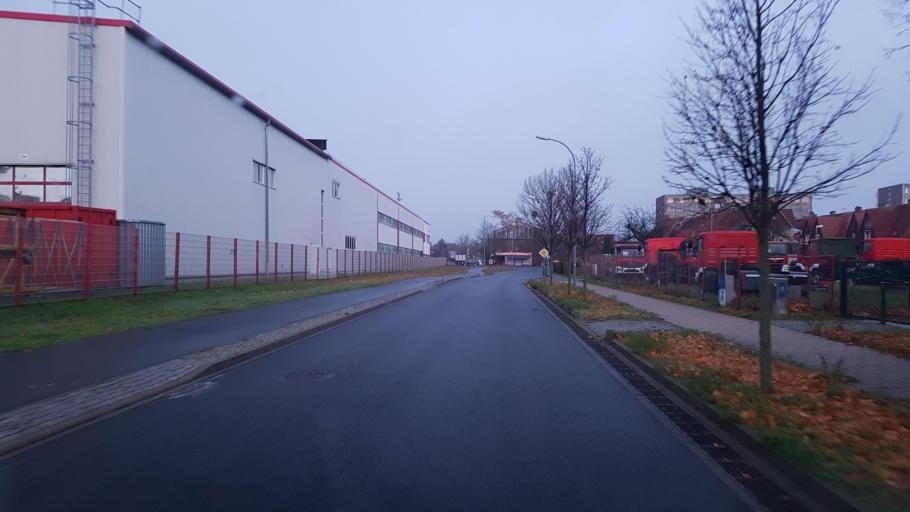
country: DE
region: Brandenburg
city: Luckenwalde
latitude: 52.0820
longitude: 13.1560
